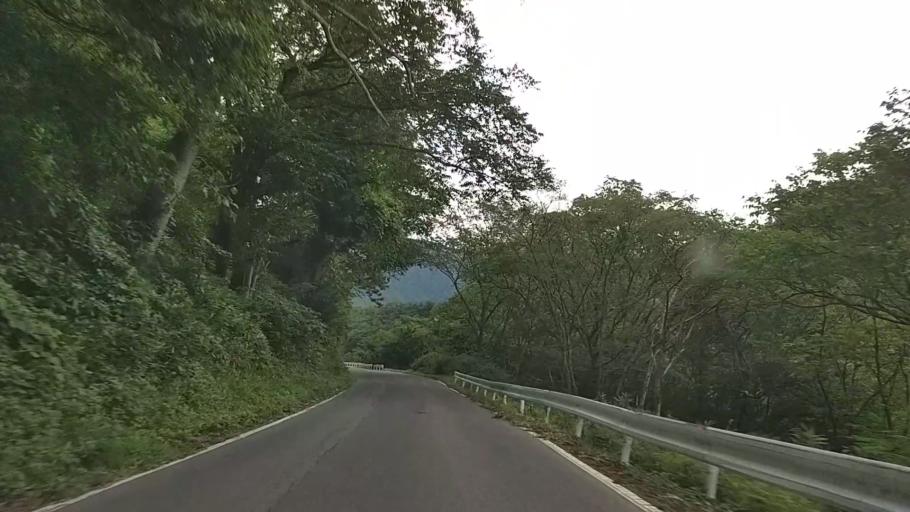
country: JP
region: Nagano
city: Nakano
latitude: 36.7918
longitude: 138.3426
